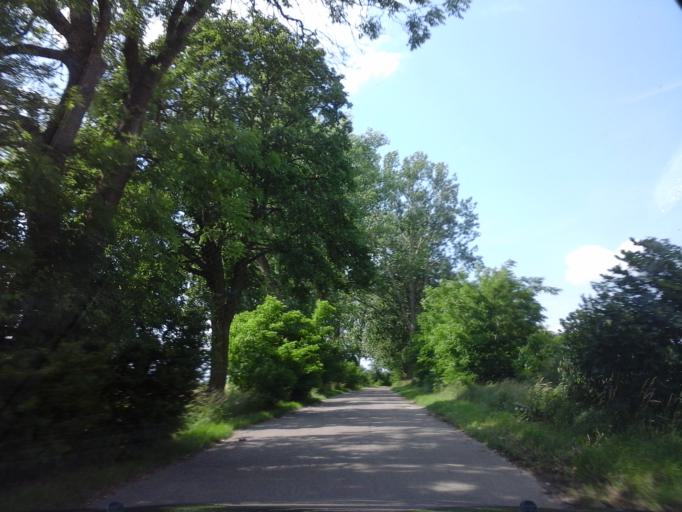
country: PL
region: West Pomeranian Voivodeship
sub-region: Powiat choszczenski
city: Choszczno
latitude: 53.1138
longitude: 15.4007
